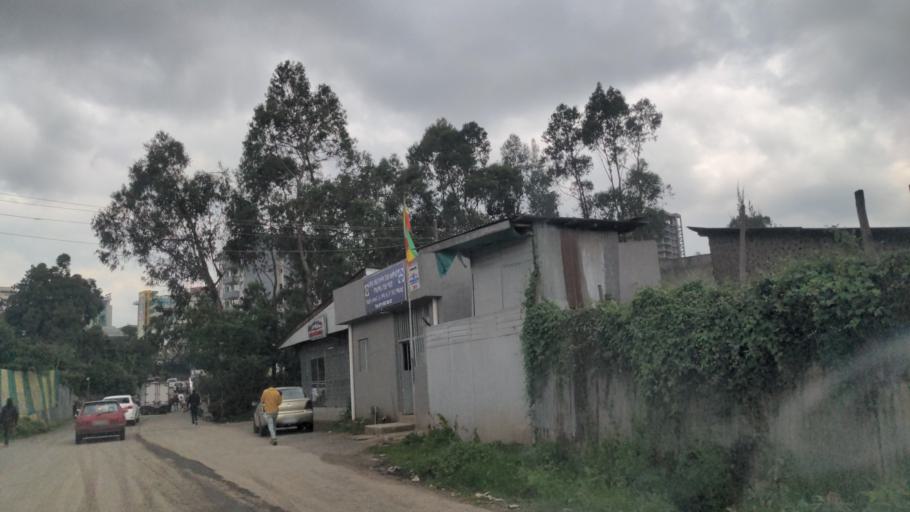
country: ET
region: Adis Abeba
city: Addis Ababa
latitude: 9.0136
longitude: 38.7905
